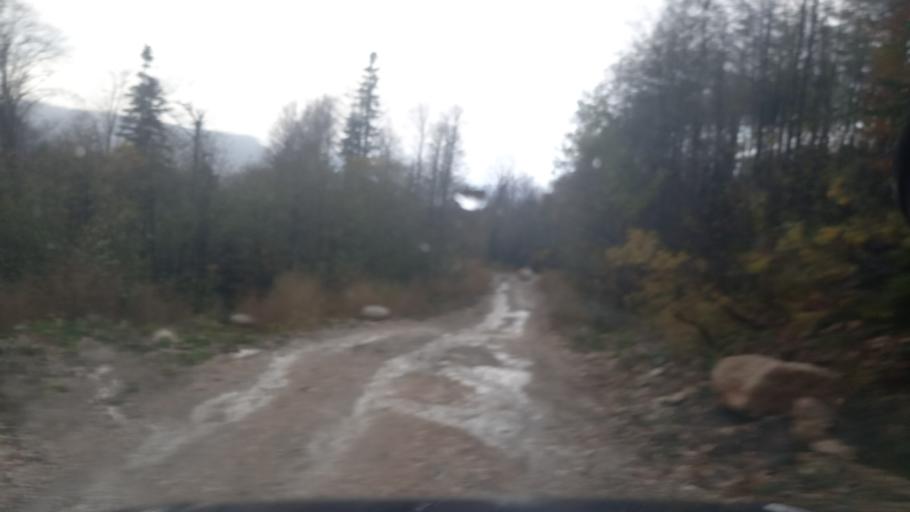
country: RU
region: Krasnodarskiy
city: Dagomys
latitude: 43.9979
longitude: 39.8530
